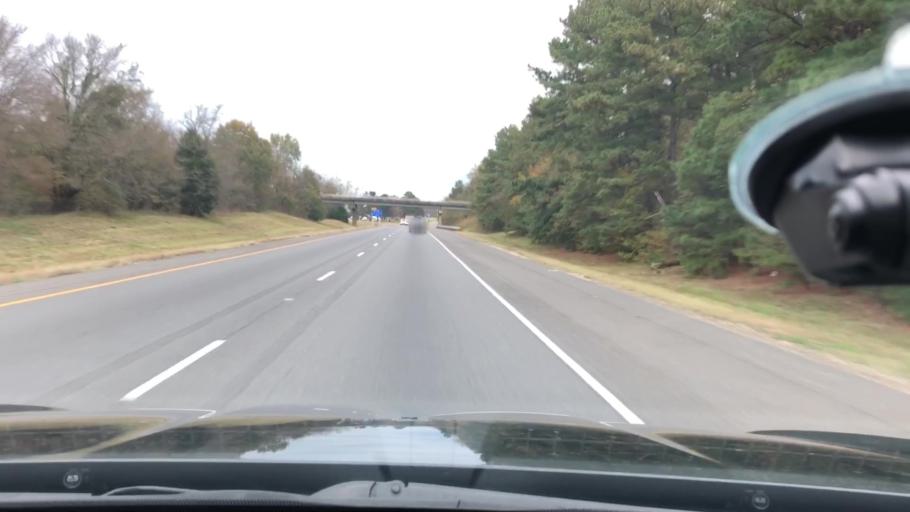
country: US
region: Arkansas
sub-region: Hot Spring County
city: Malvern
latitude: 34.3467
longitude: -92.8979
